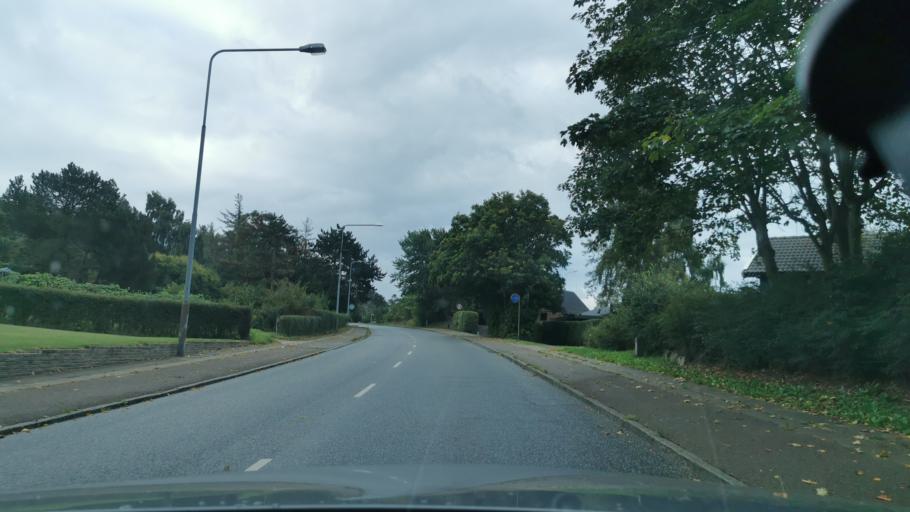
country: DK
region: Zealand
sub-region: Kalundborg Kommune
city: Kalundborg
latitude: 55.7041
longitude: 11.0241
